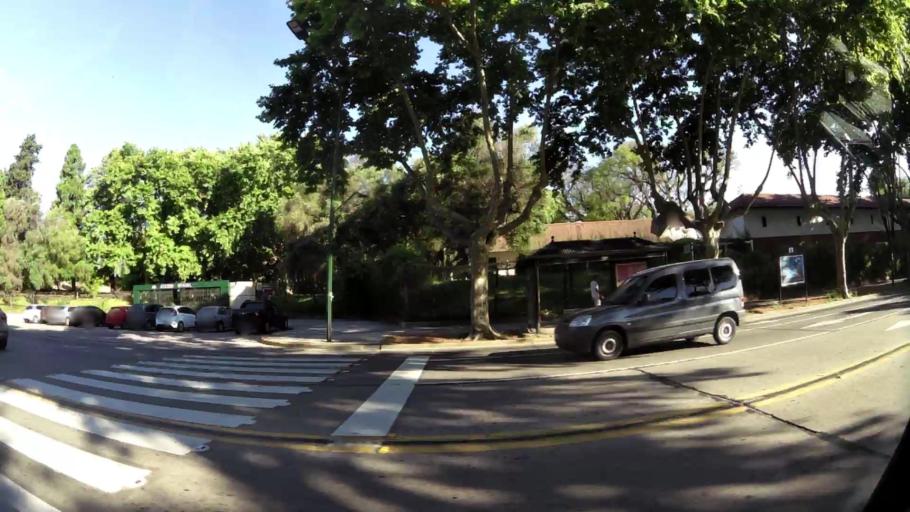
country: AR
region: Buenos Aires
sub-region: Partido de San Isidro
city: San Isidro
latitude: -34.4803
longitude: -58.5243
